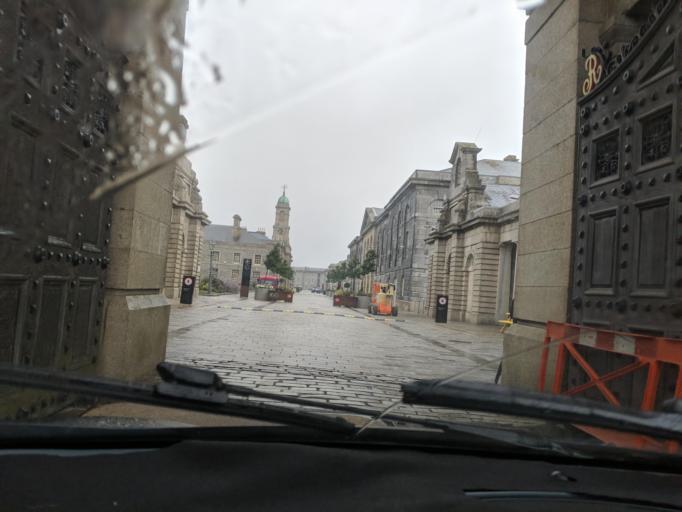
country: GB
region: England
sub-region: Cornwall
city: Millbrook
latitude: 50.3625
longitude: -4.1628
